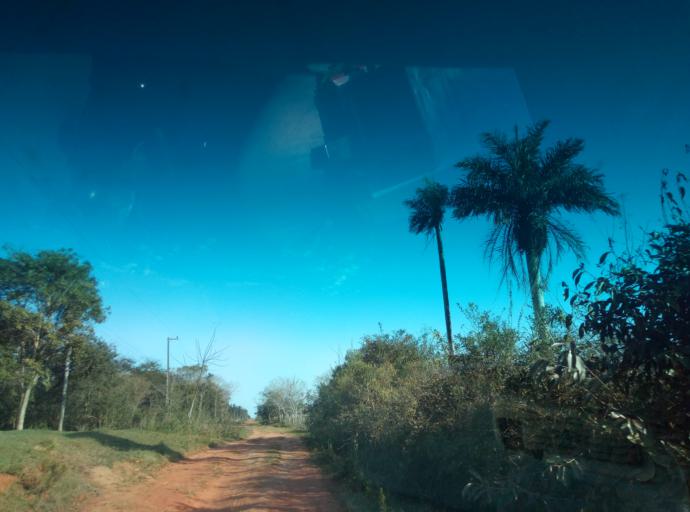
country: PY
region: Caaguazu
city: Doctor Cecilio Baez
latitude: -25.1652
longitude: -56.2320
